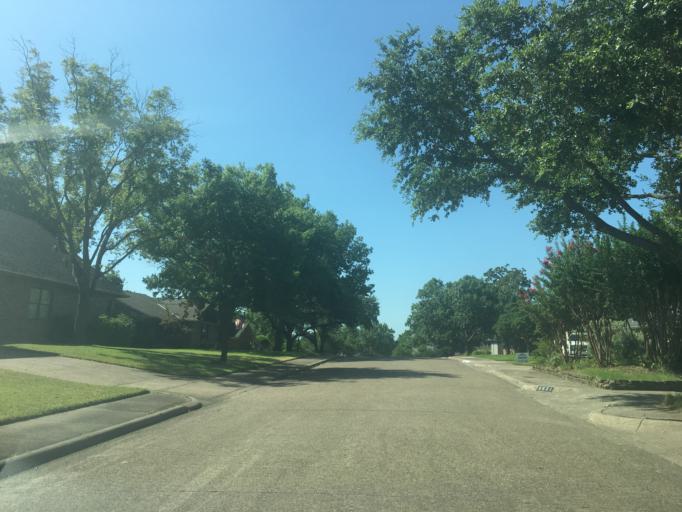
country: US
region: Texas
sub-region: Dallas County
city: Richardson
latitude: 32.8765
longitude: -96.7285
